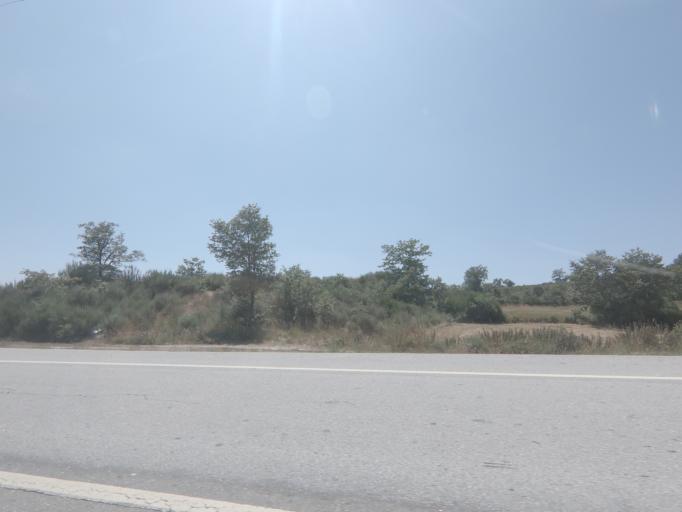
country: PT
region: Viseu
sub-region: Tarouca
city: Tarouca
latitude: 41.0018
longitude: -7.8872
